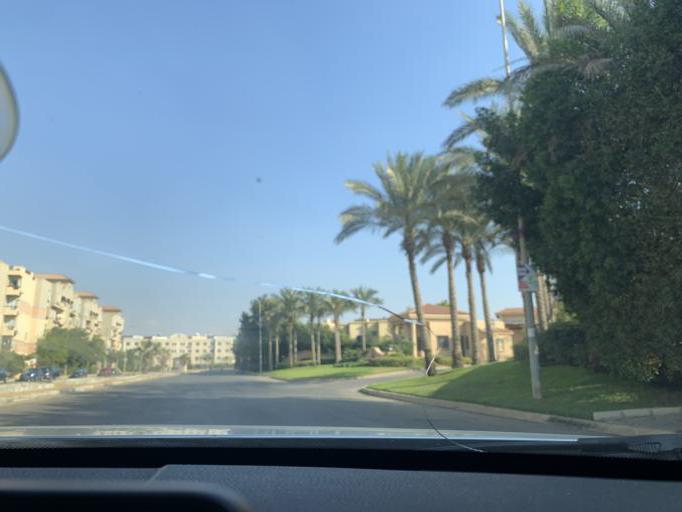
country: EG
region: Muhafazat al Qalyubiyah
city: Al Khankah
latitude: 30.0187
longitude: 31.4835
